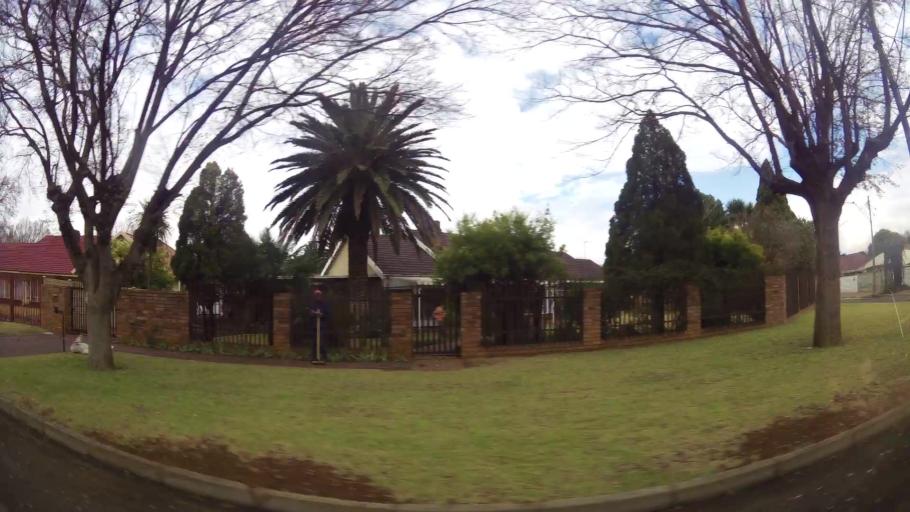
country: ZA
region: Gauteng
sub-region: Sedibeng District Municipality
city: Vereeniging
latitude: -26.6436
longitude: 27.9817
